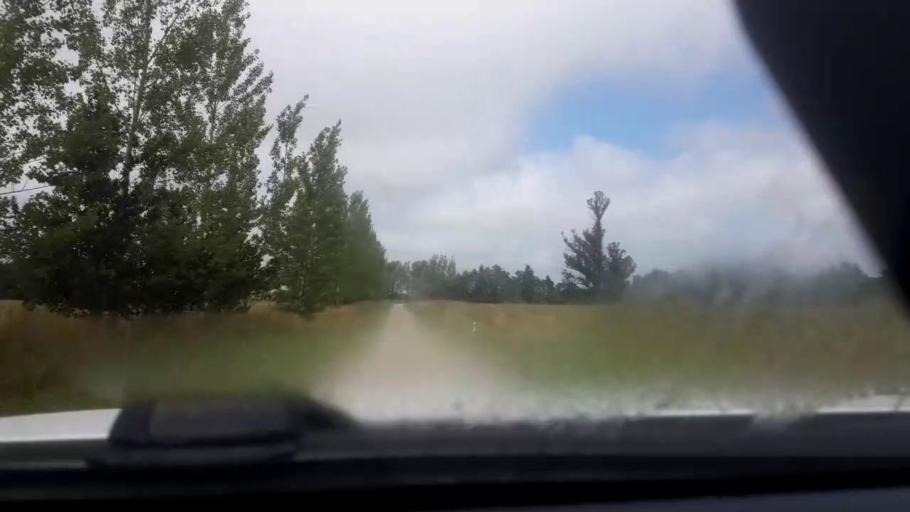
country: NZ
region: Canterbury
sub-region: Timaru District
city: Pleasant Point
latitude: -44.2004
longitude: 171.0902
